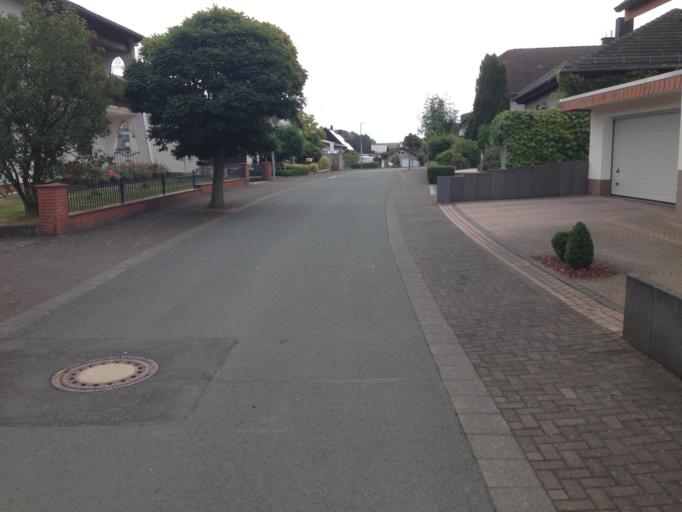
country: DE
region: Hesse
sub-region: Regierungsbezirk Giessen
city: Lohra
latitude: 50.6700
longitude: 8.5671
